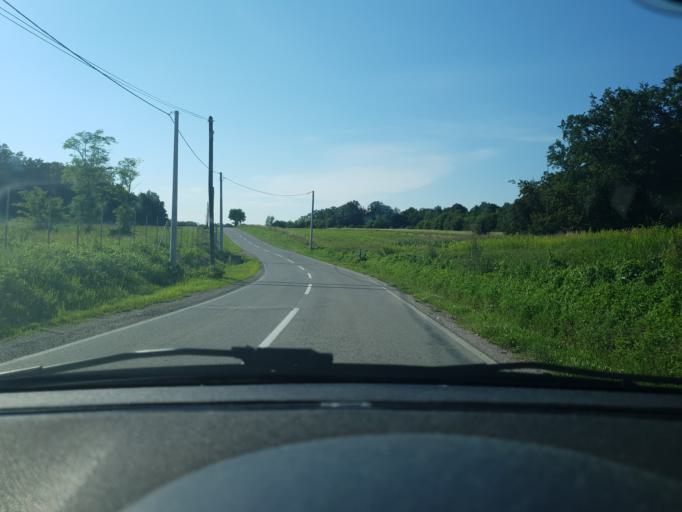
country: HR
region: Zagrebacka
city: Jablanovec
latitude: 45.9136
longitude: 15.8462
